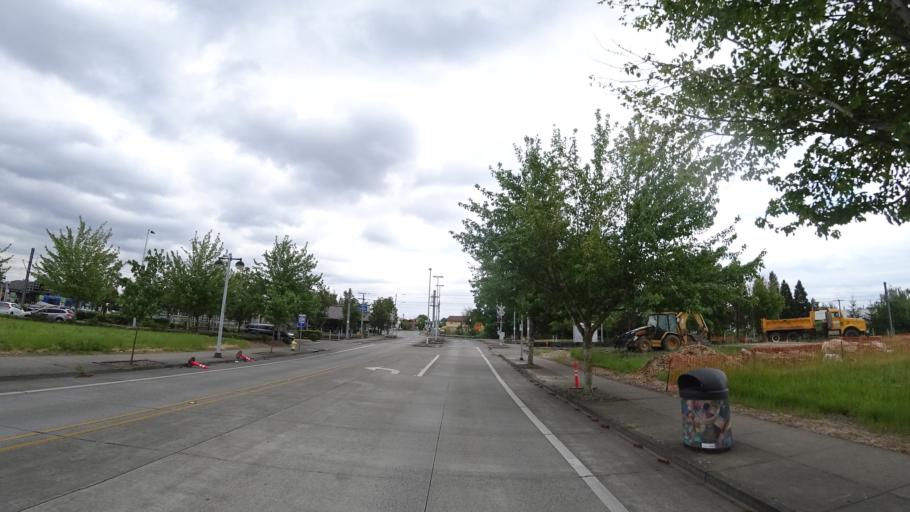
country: US
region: Oregon
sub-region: Washington County
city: Beaverton
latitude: 45.4914
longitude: -122.8026
